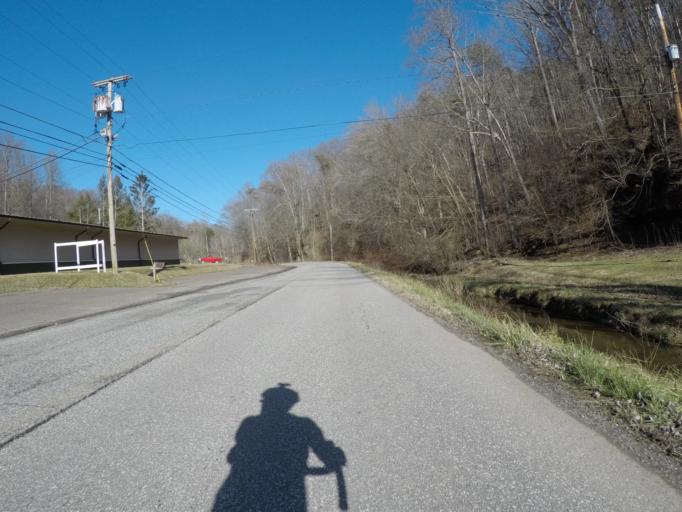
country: US
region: Kentucky
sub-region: Boyd County
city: Catlettsburg
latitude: 38.4214
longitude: -82.6387
